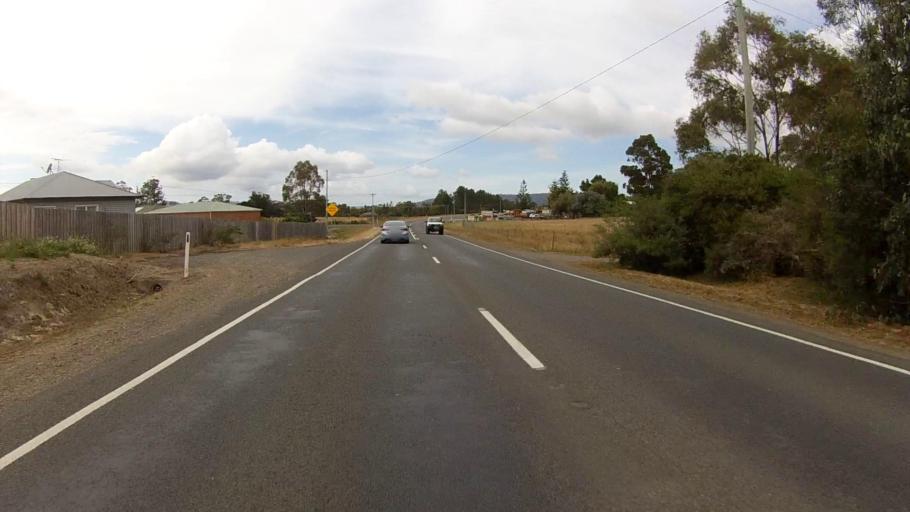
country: AU
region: Tasmania
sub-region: Kingborough
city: Margate
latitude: -43.0335
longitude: 147.2654
